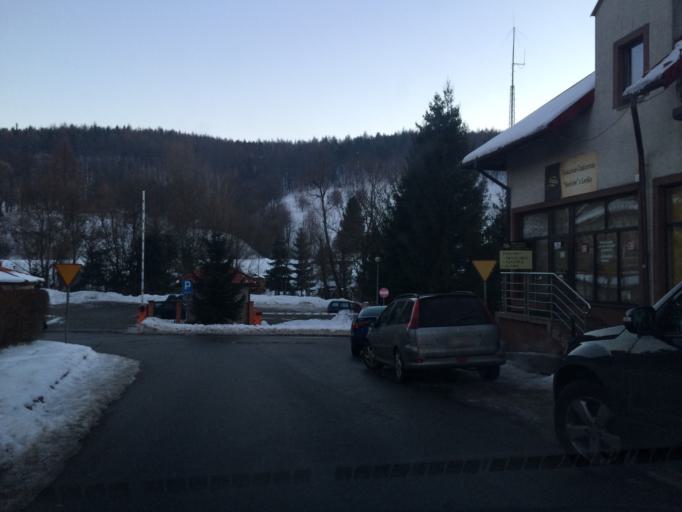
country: PL
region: Subcarpathian Voivodeship
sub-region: Powiat bieszczadzki
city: Ustrzyki Dolne
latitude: 49.4294
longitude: 22.5871
